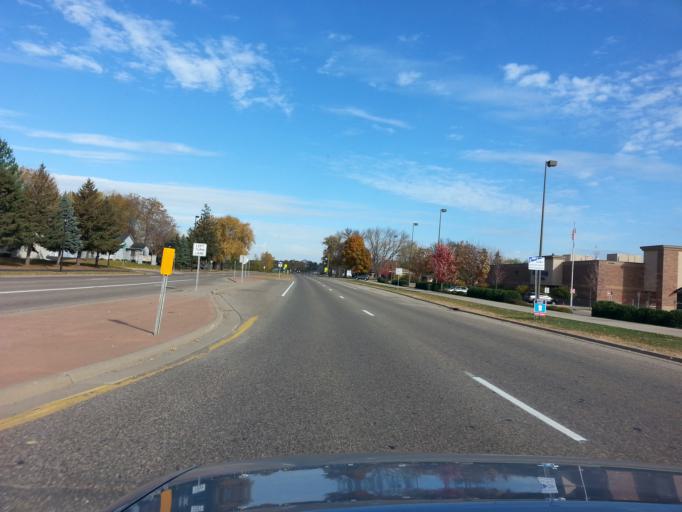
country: US
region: Minnesota
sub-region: Dakota County
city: Lakeville
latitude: 44.6580
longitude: -93.2527
